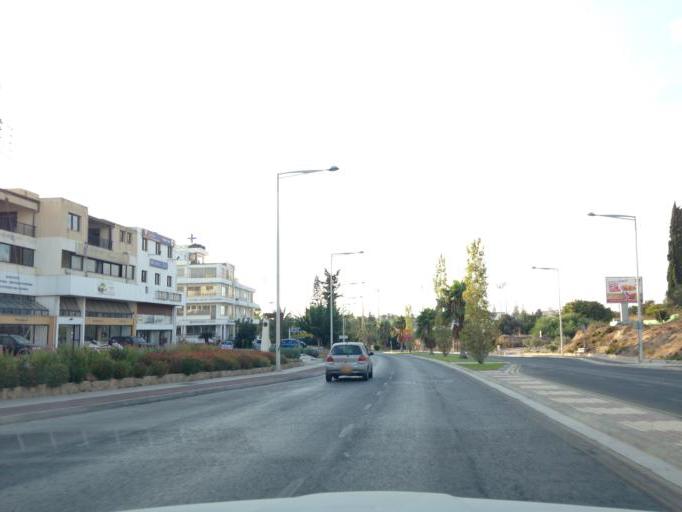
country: CY
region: Pafos
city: Paphos
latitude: 34.7668
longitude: 32.4442
